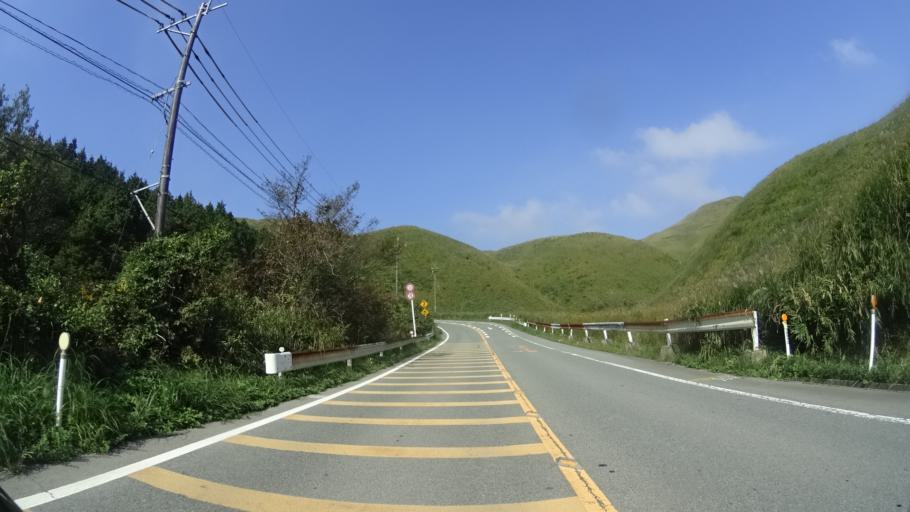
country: JP
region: Kumamoto
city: Aso
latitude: 32.9197
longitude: 130.9681
